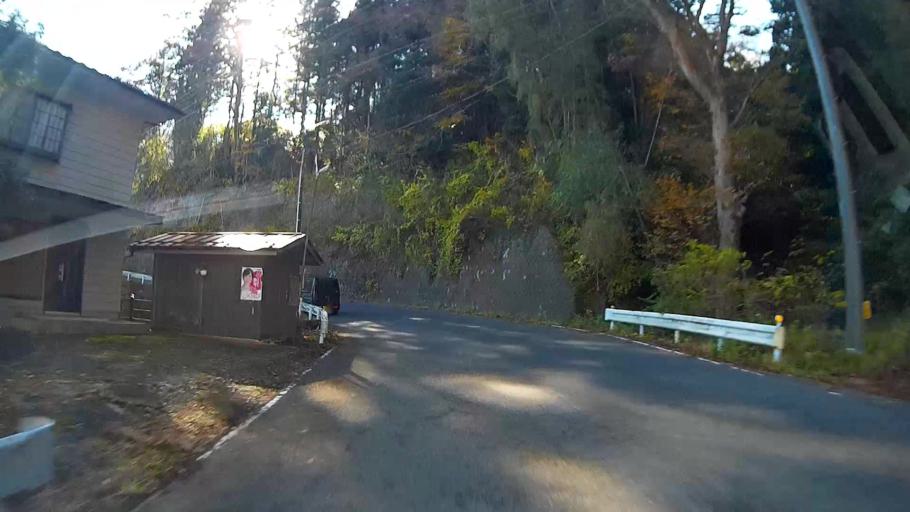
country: JP
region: Yamanashi
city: Uenohara
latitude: 35.5708
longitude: 139.0905
